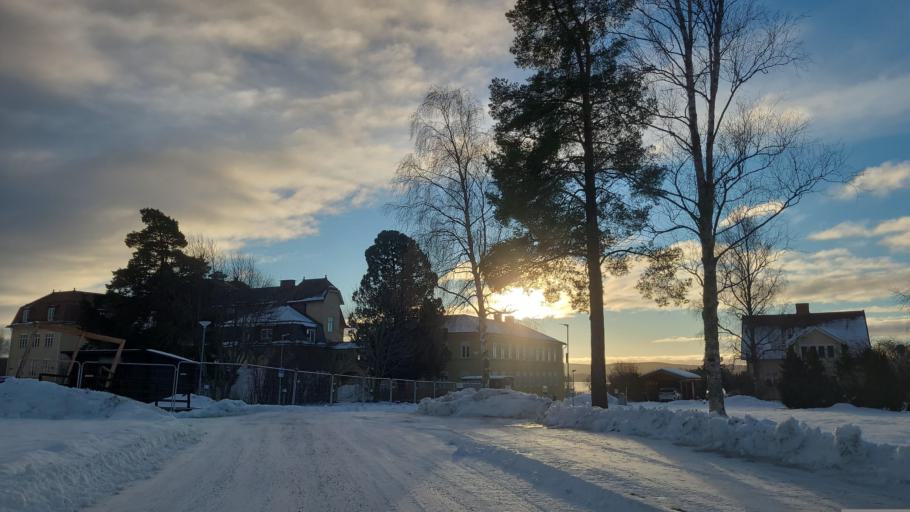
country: SE
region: Gaevleborg
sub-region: Bollnas Kommun
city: Bollnas
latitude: 61.3586
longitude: 16.4239
